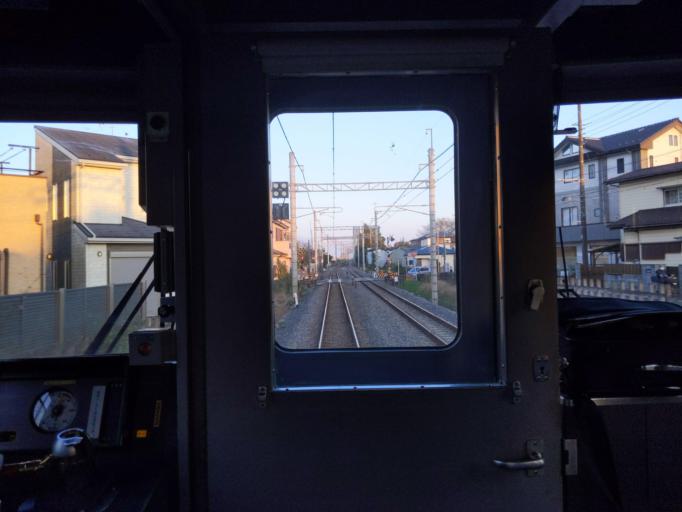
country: JP
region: Chiba
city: Noda
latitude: 35.9810
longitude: 139.8172
